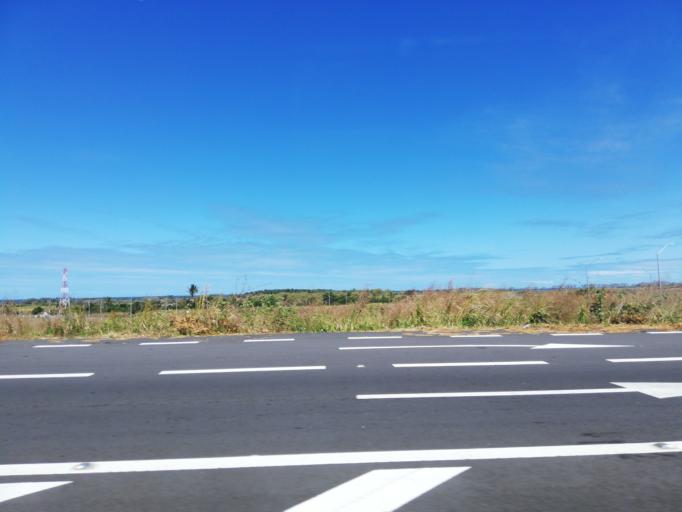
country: MU
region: Grand Port
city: Plaine Magnien
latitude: -20.4429
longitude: 57.6888
